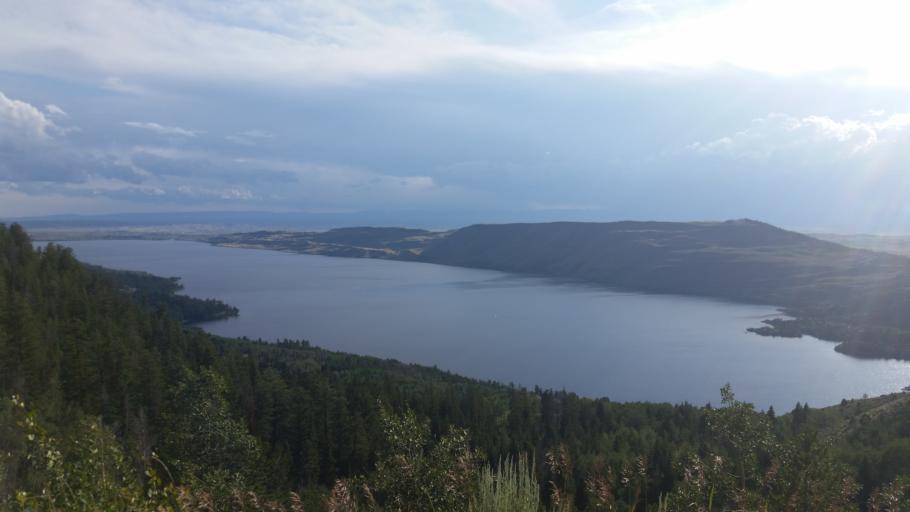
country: US
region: Wyoming
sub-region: Sublette County
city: Pinedale
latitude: 42.9709
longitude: -109.7667
